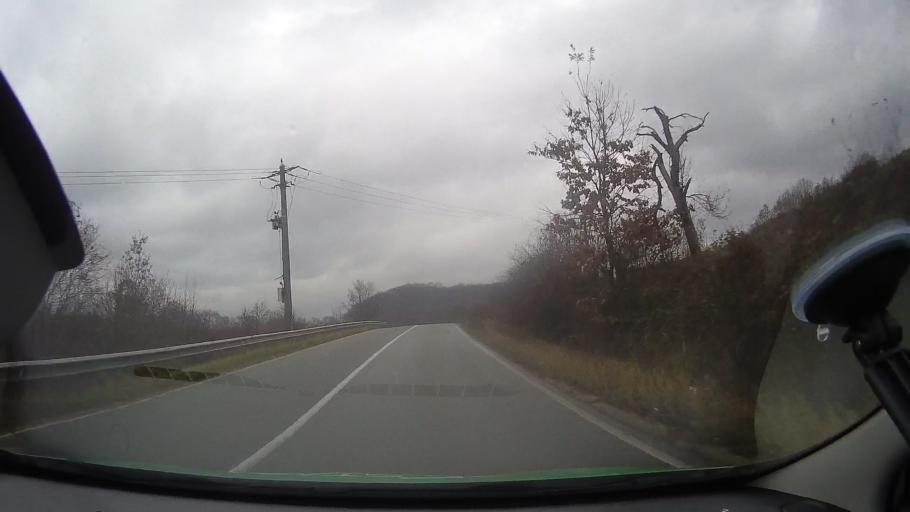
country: RO
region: Arad
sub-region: Comuna Almas
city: Almas
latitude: 46.3004
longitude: 22.1896
